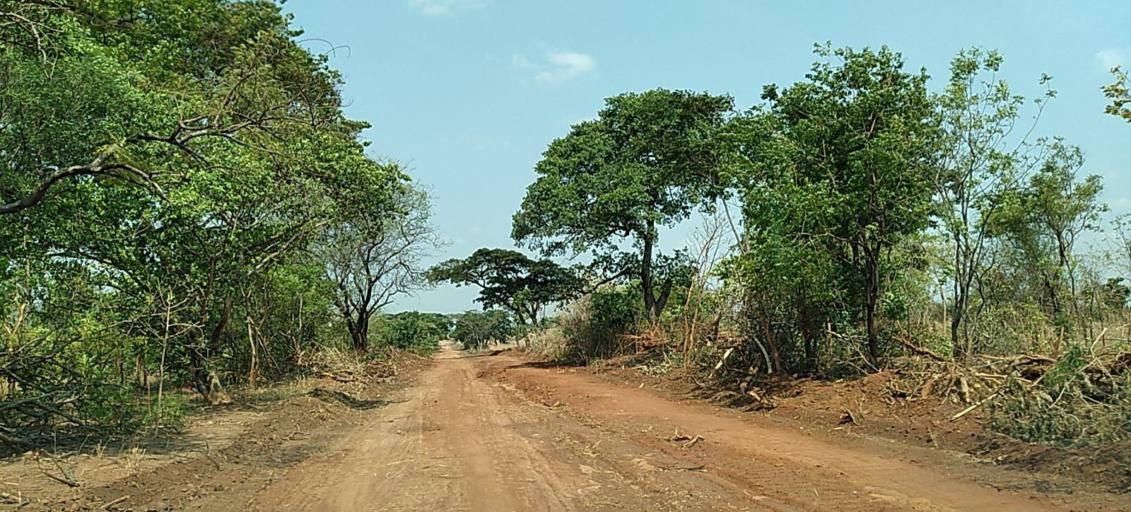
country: ZM
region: Copperbelt
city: Luanshya
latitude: -13.0902
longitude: 28.2748
